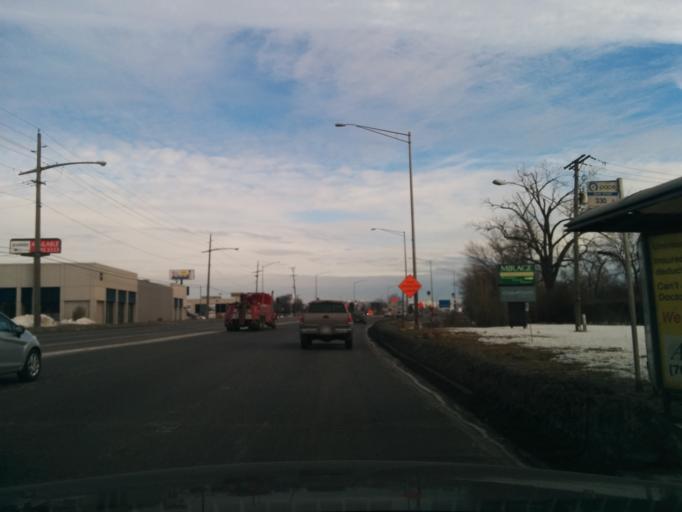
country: US
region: Illinois
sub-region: Cook County
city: Schiller Park
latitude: 41.9543
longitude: -87.8856
